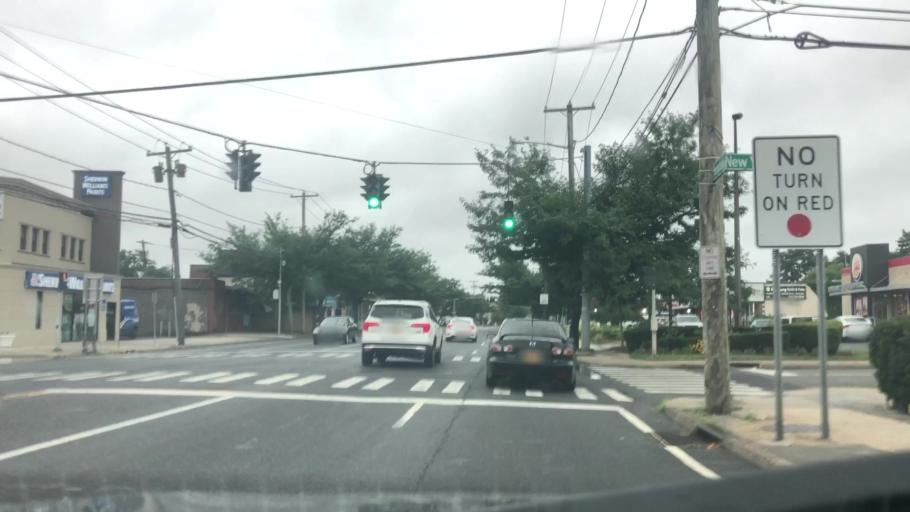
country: US
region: New York
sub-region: Nassau County
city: West Hempstead
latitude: 40.7051
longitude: -73.6510
